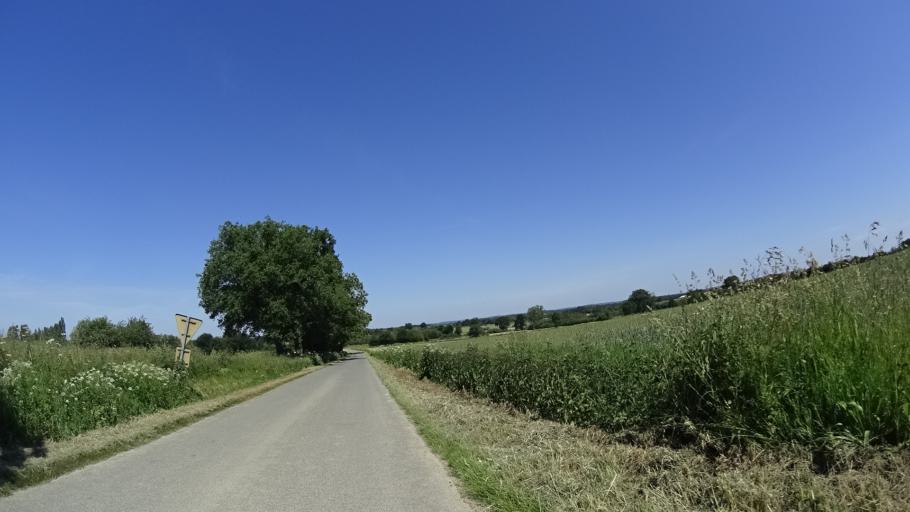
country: FR
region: Brittany
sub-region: Departement d'Ille-et-Vilaine
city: Messac
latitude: 47.7860
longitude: -1.8067
